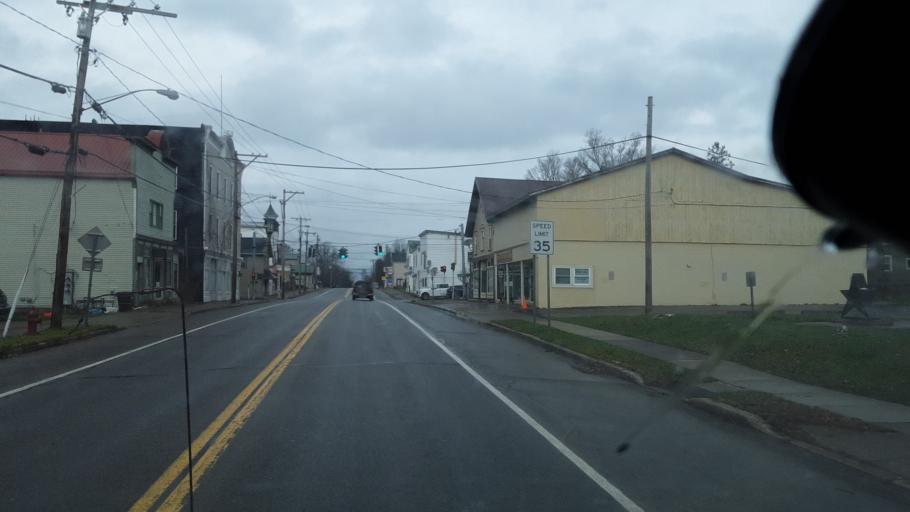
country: US
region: New York
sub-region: Cattaraugus County
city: Delevan
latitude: 42.4885
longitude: -78.4803
